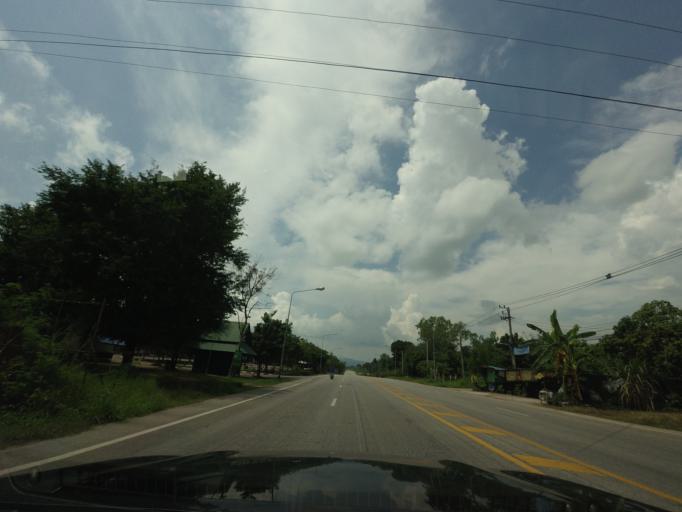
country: TH
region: Khon Kaen
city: Phu Wiang
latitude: 16.6788
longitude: 102.3414
